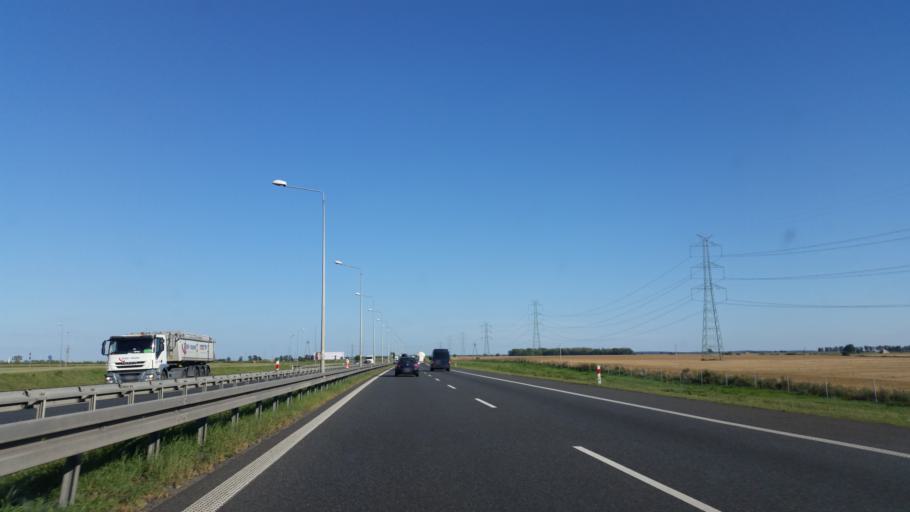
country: PL
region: Opole Voivodeship
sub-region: Powiat brzeski
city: Olszanka
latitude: 50.7563
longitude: 17.4313
